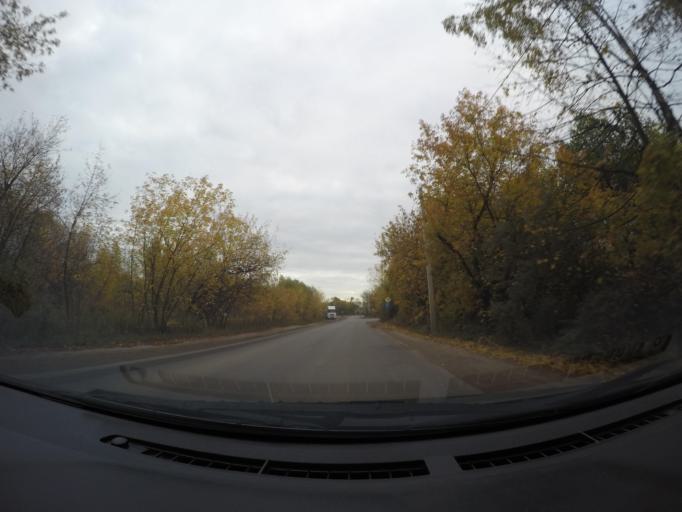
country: RU
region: Moskovskaya
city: Staraya Kupavna
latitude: 55.7964
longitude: 38.1809
